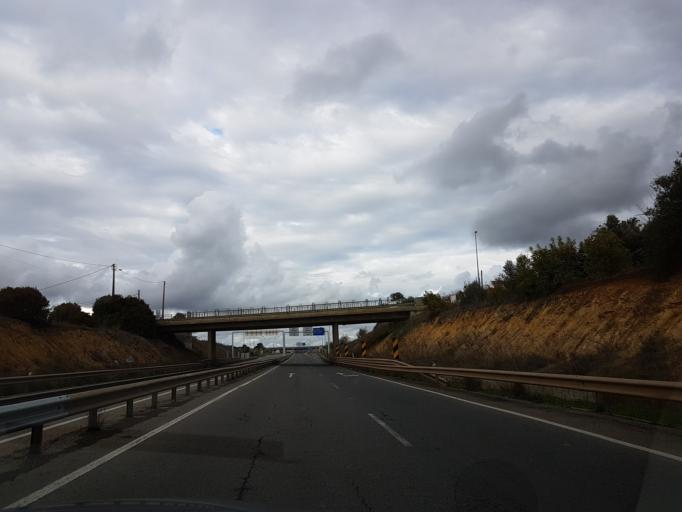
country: PT
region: Faro
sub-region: Albufeira
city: Ferreiras
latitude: 37.1311
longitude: -8.2570
